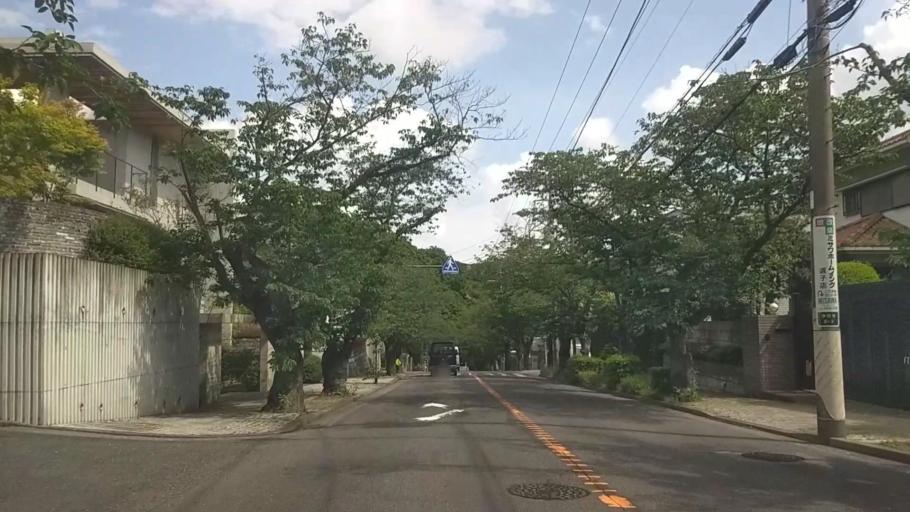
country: JP
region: Kanagawa
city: Zushi
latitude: 35.3159
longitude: 139.5767
